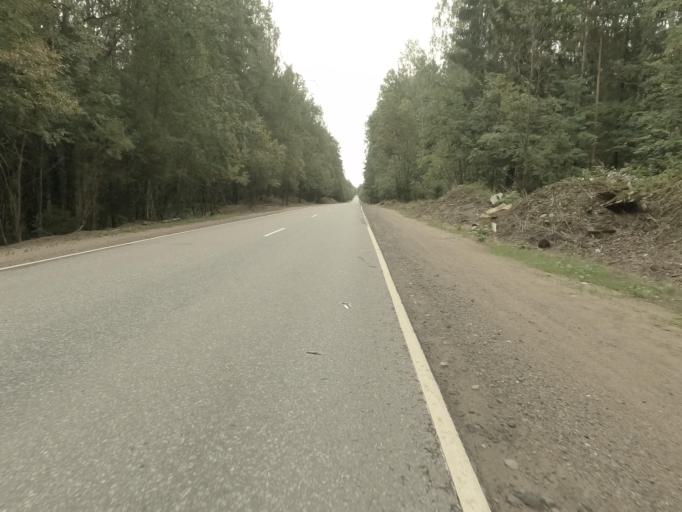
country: RU
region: Leningrad
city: Koltushi
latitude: 59.8979
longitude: 30.7589
